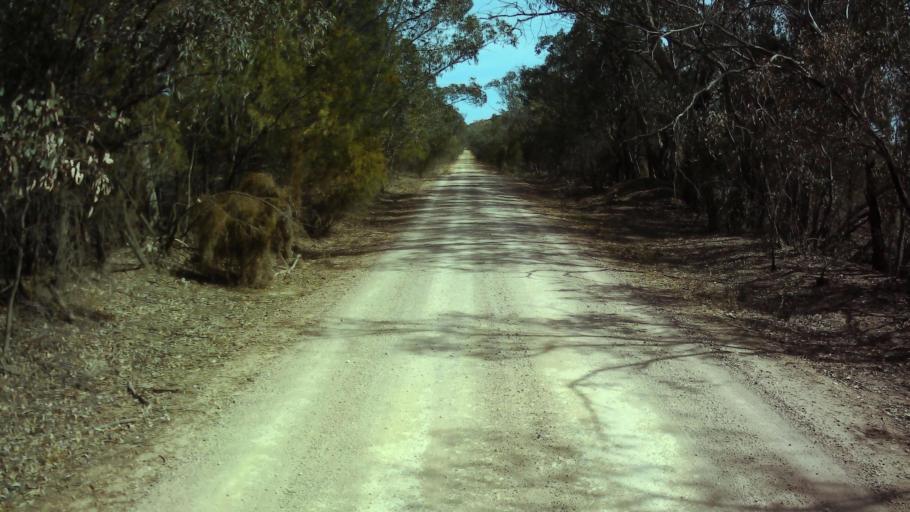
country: AU
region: New South Wales
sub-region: Weddin
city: Grenfell
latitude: -33.8792
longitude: 148.1503
